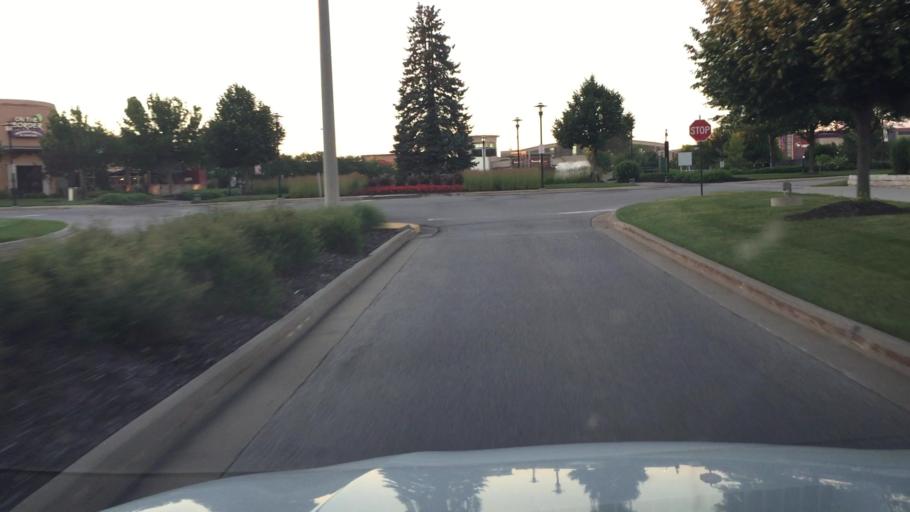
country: US
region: Iowa
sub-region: Polk County
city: Clive
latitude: 41.5657
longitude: -93.8041
